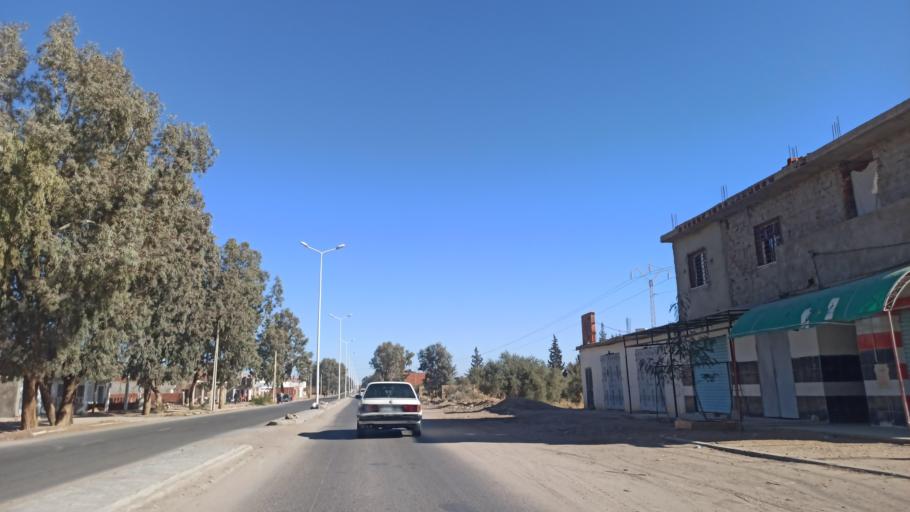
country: TN
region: Gafsa
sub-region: Gafsa Municipality
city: Gafsa
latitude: 34.4022
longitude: 8.7258
